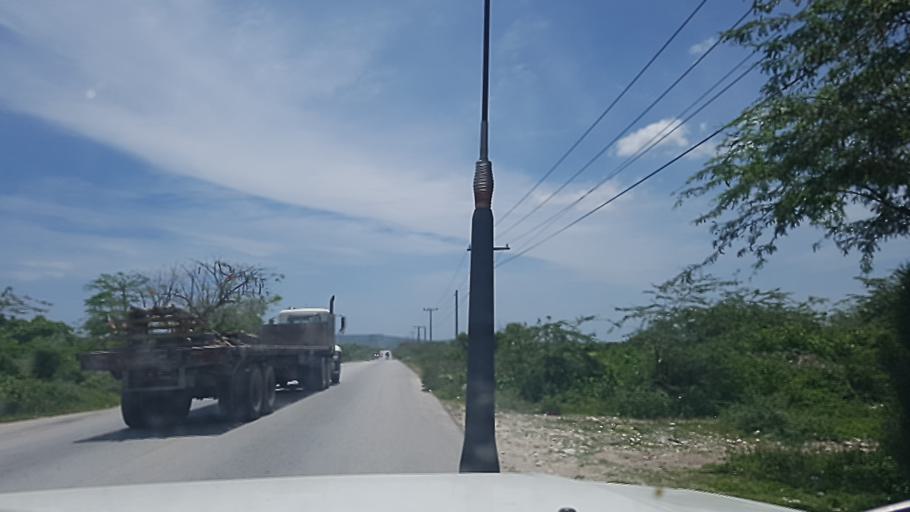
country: HT
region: Artibonite
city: Saint-Marc
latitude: 19.1518
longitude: -72.6274
